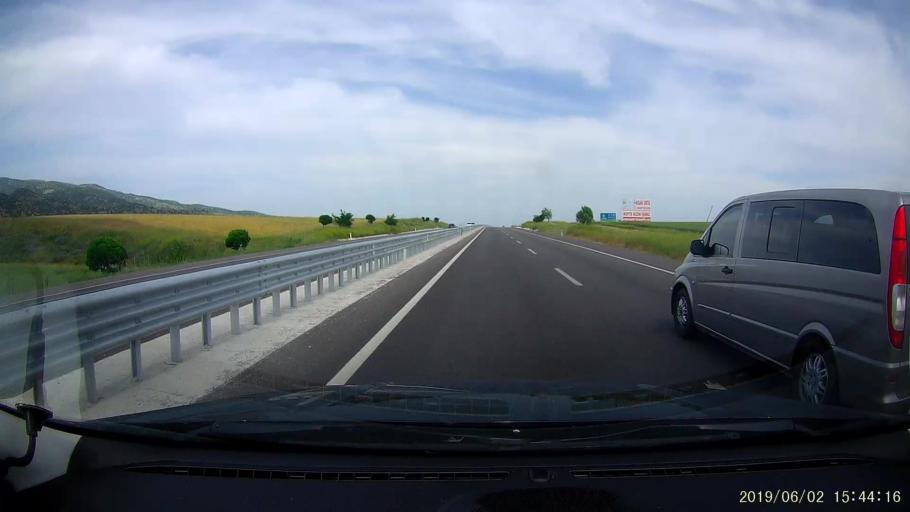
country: TR
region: Amasya
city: Alicik
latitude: 40.8657
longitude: 35.3516
